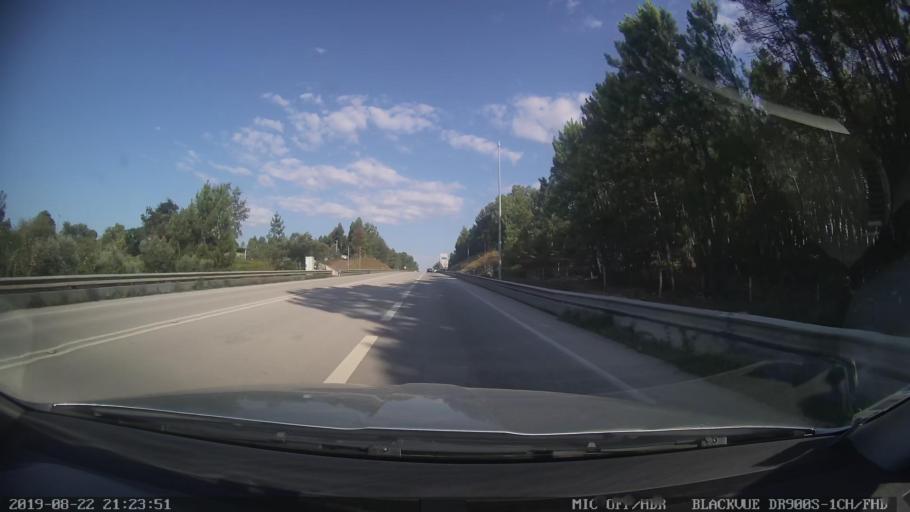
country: PT
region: Castelo Branco
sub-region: Serta
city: Serta
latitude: 39.8357
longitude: -8.1133
